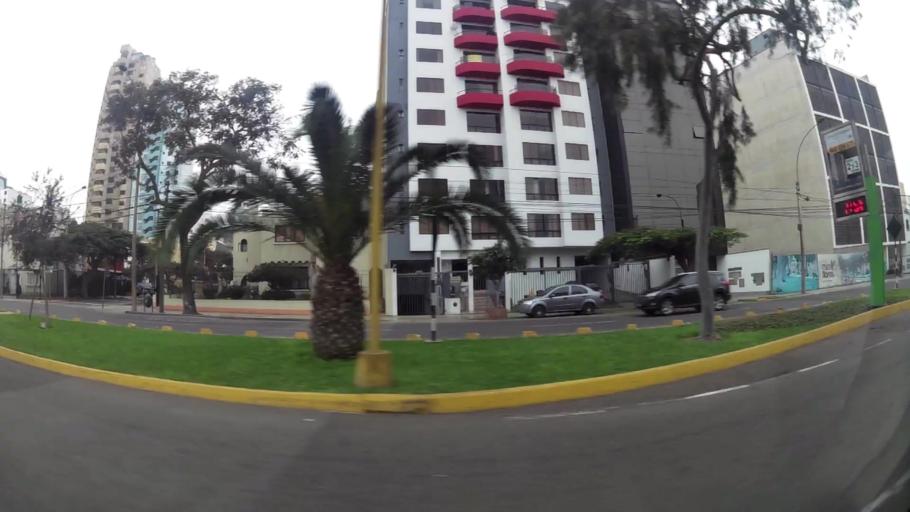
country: PE
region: Lima
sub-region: Lima
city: Surco
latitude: -12.1319
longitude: -77.0236
